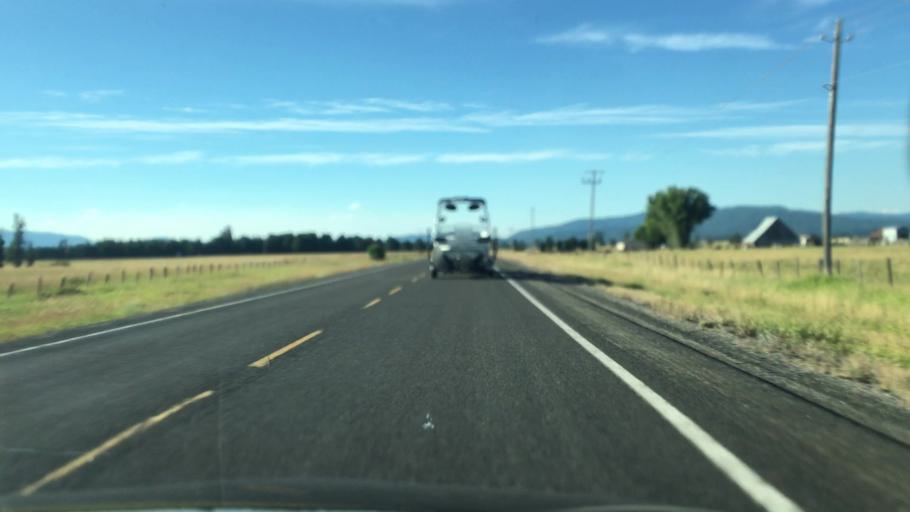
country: US
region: Idaho
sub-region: Valley County
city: Cascade
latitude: 44.4409
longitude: -115.9994
